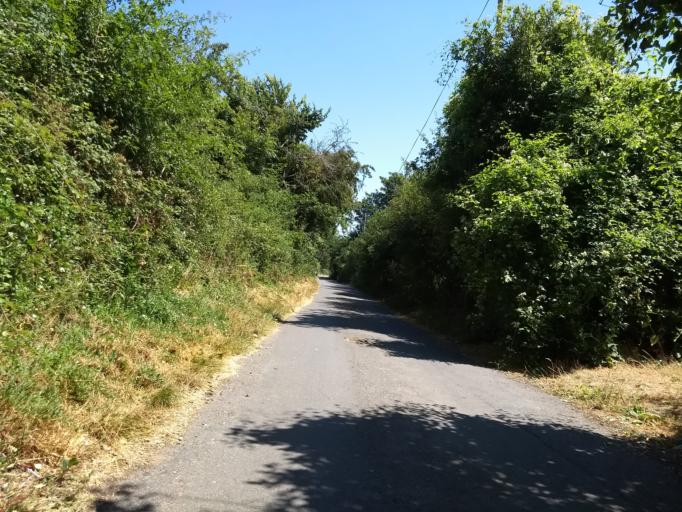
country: GB
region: England
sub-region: Isle of Wight
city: Brading
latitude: 50.6819
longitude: -1.1345
